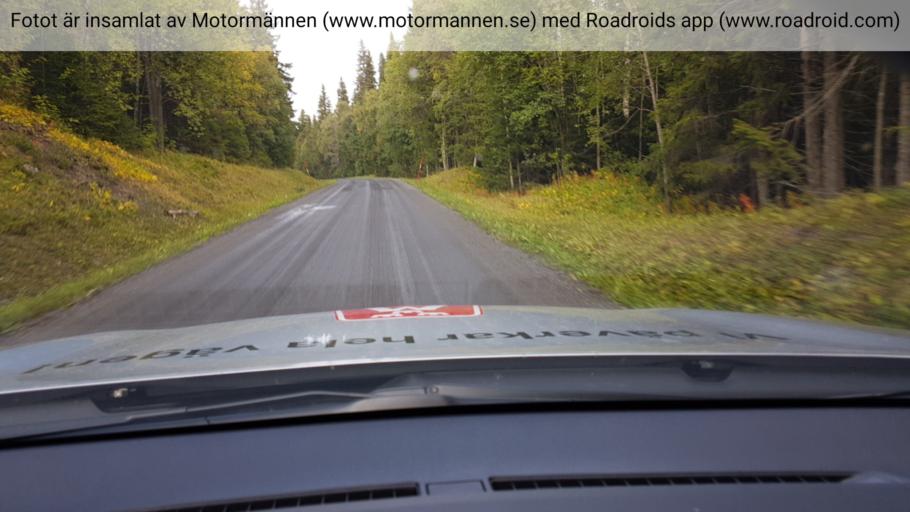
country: SE
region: Jaemtland
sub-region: Stroemsunds Kommun
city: Stroemsund
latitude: 64.0958
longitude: 15.8273
